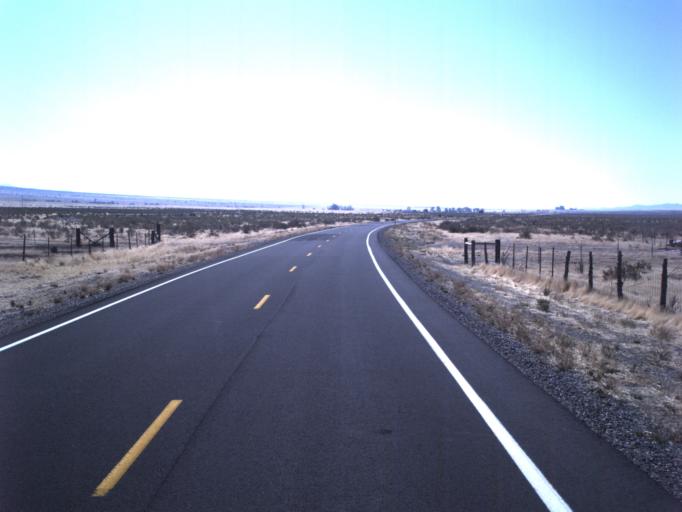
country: US
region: Utah
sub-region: Tooele County
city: Grantsville
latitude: 40.4851
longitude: -112.7458
